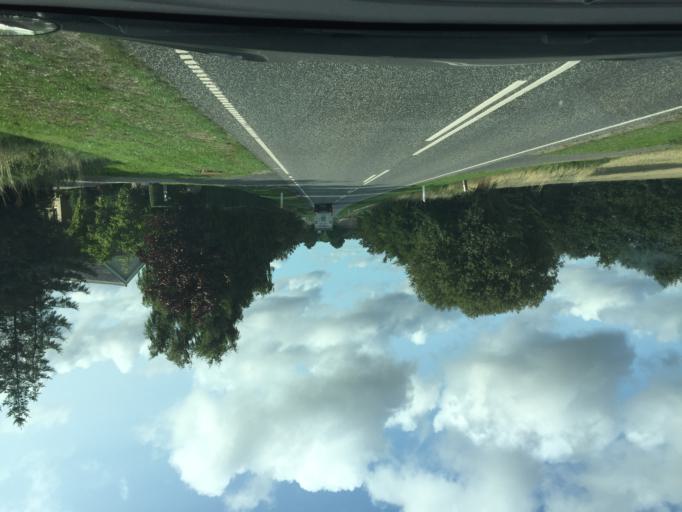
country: DK
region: Central Jutland
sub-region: Odder Kommune
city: Odder
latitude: 55.9035
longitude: 10.0251
